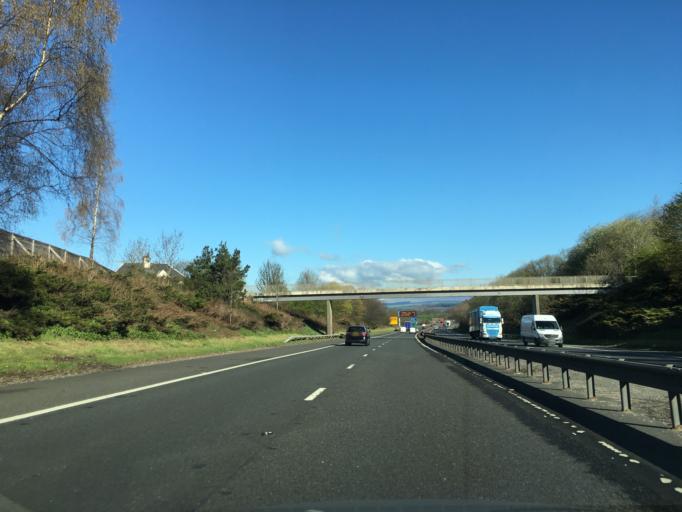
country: GB
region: Scotland
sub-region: Stirling
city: Stirling
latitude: 56.1114
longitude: -3.9637
